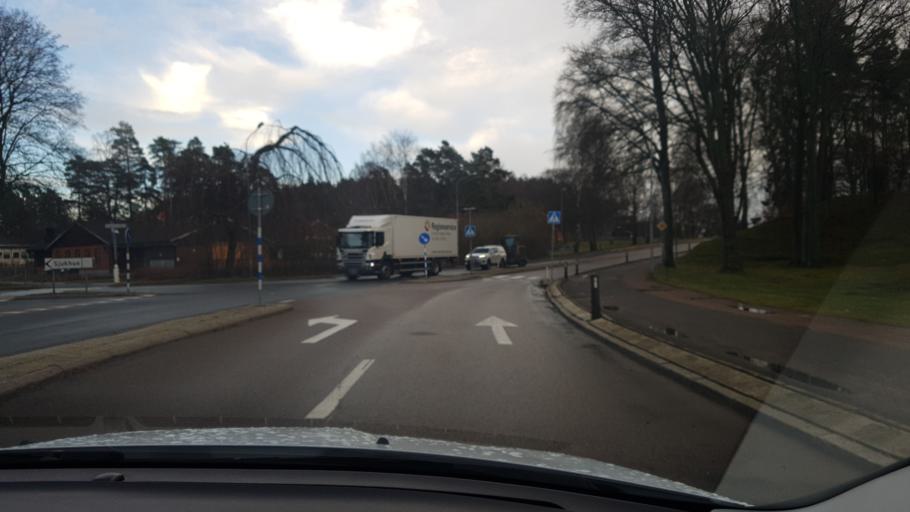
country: SE
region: Skane
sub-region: Hassleholms Kommun
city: Hassleholm
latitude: 56.1558
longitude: 13.7773
